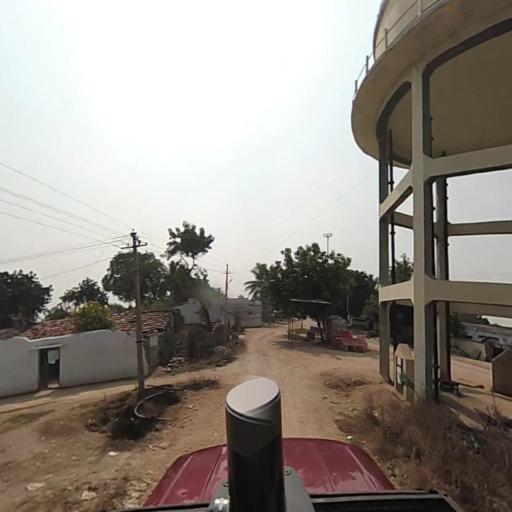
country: IN
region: Telangana
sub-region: Nalgonda
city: Nalgonda
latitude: 17.1912
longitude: 79.1310
